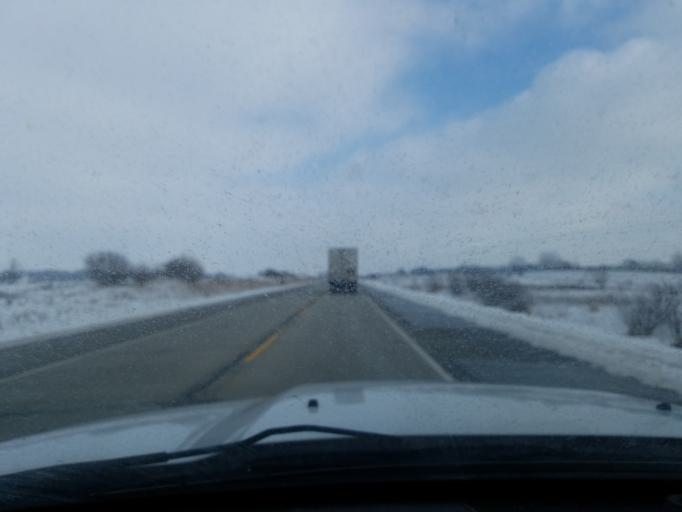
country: US
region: Indiana
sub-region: Marshall County
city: Bremen
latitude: 41.4607
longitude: -86.1684
